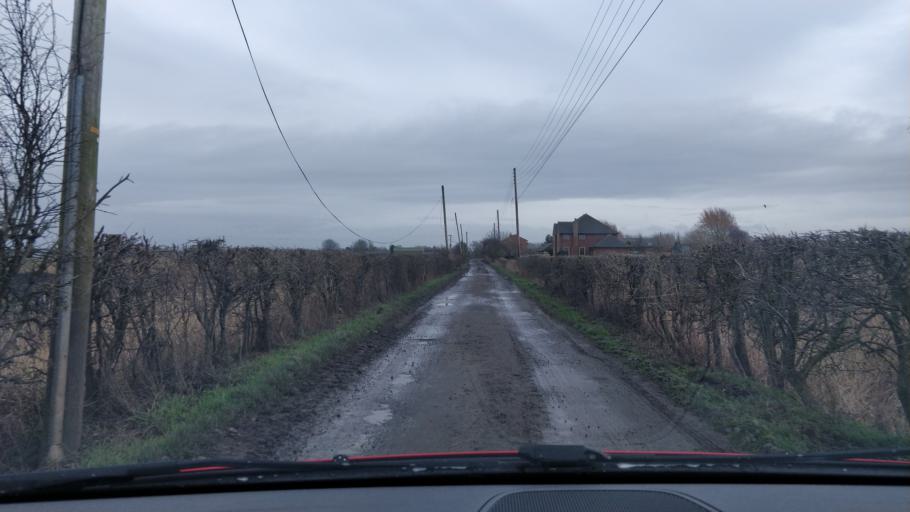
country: GB
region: England
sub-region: Lancashire
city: Banks
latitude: 53.6862
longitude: -2.9330
